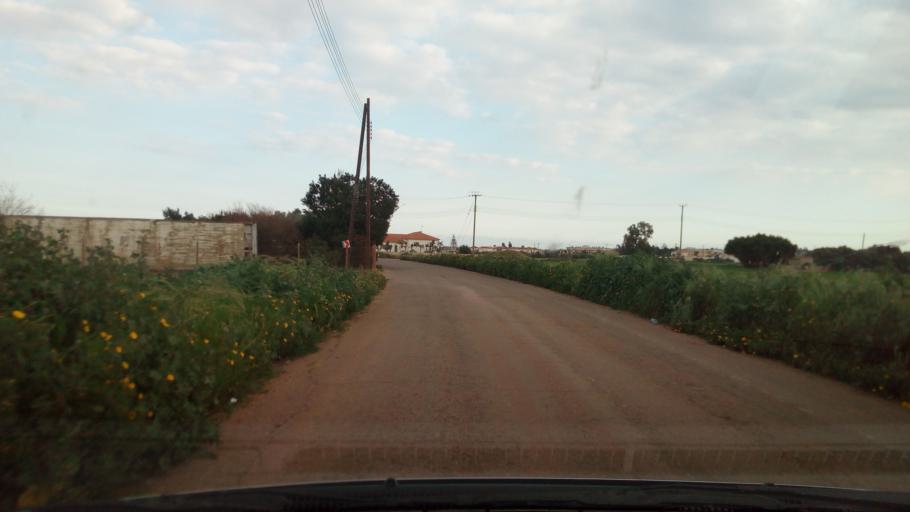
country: CY
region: Ammochostos
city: Avgorou
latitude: 34.9832
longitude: 33.8384
